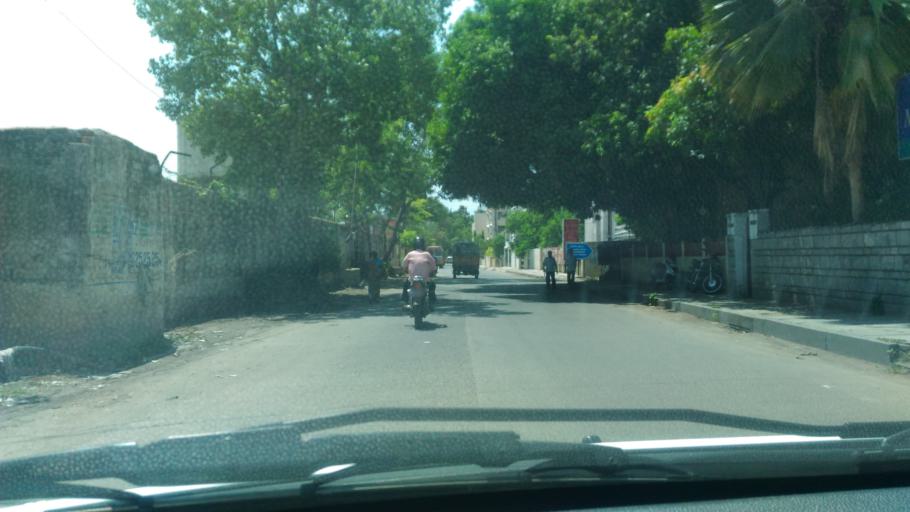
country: IN
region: Tamil Nadu
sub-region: Chennai
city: Chetput
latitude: 13.0517
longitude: 80.2436
